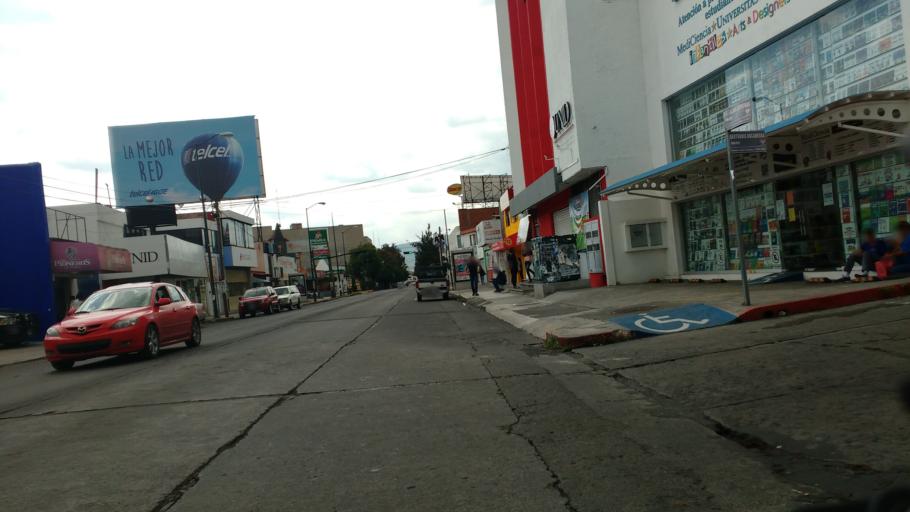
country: MX
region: Michoacan
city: Morelia
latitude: 19.6943
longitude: -101.1828
